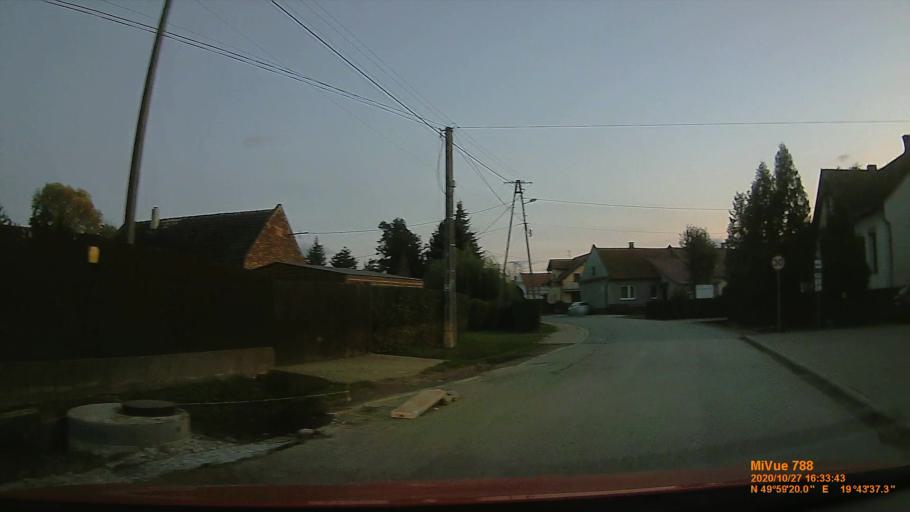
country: PL
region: Lesser Poland Voivodeship
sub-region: Powiat krakowski
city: Wolowice
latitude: 49.9889
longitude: 19.7271
